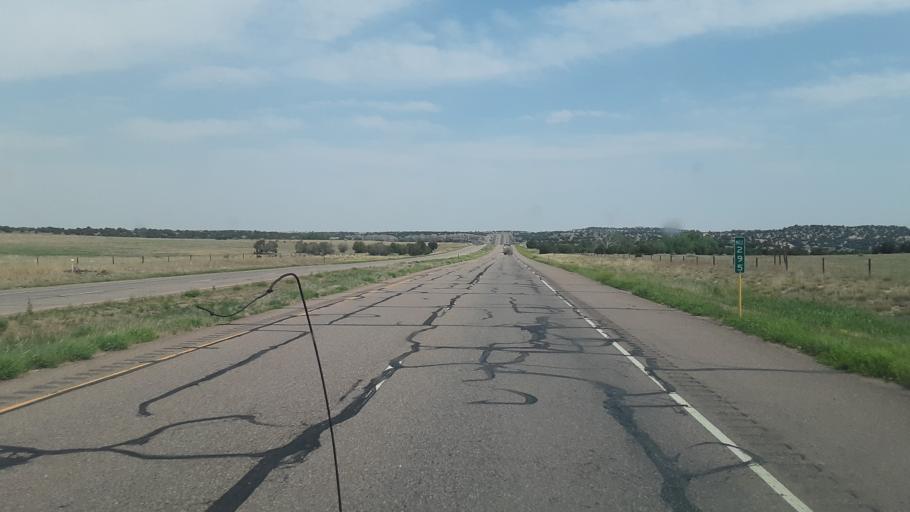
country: US
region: Colorado
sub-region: Fremont County
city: Penrose
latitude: 38.3852
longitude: -104.9598
